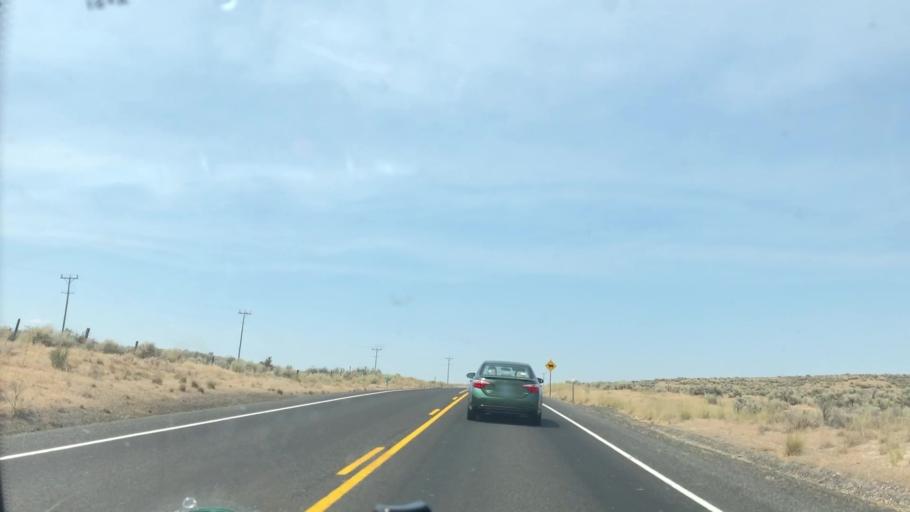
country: US
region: Idaho
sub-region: Owyhee County
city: Murphy
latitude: 42.9928
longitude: -117.0594
